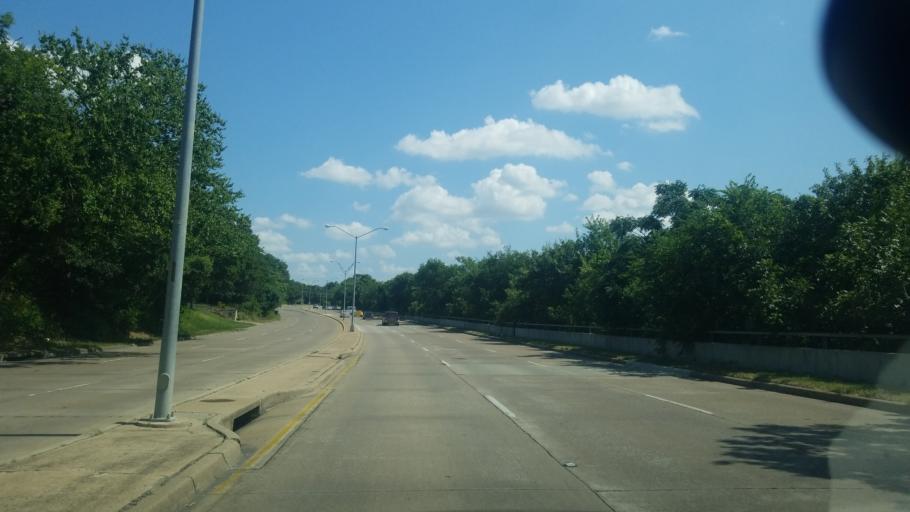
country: US
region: Texas
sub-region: Dallas County
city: Dallas
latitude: 32.7314
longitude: -96.8000
